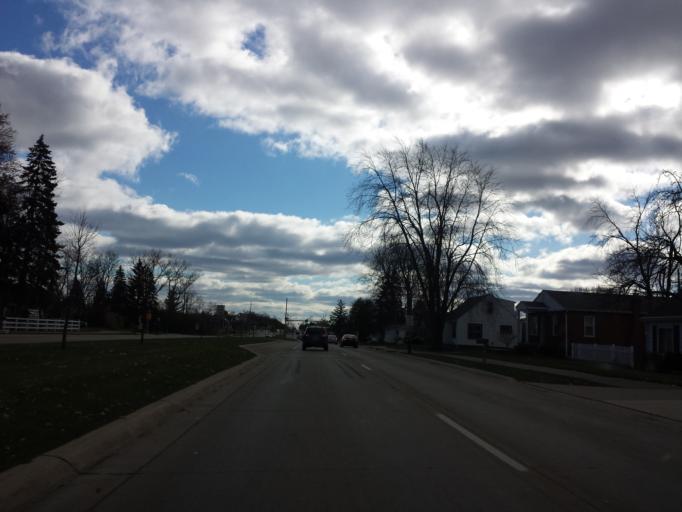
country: US
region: Michigan
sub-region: Oakland County
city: Troy
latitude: 42.6256
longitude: -83.1702
